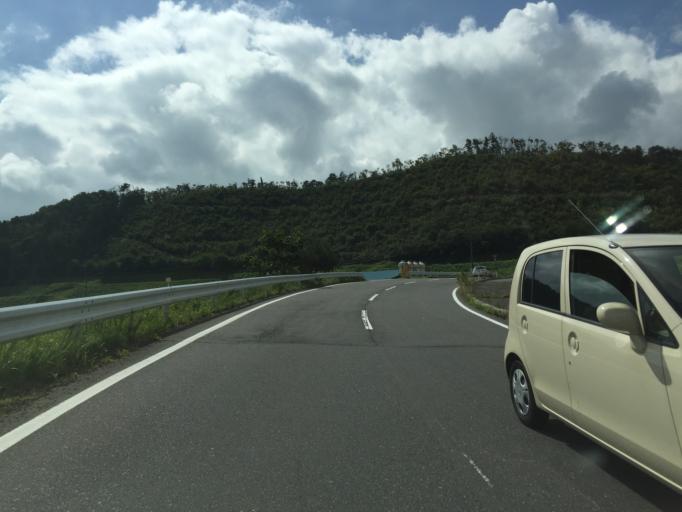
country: JP
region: Fukushima
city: Motomiya
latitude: 37.5183
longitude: 140.3736
